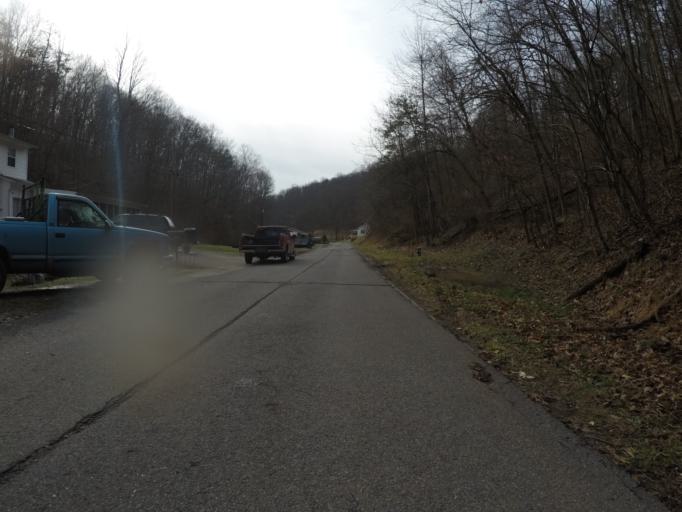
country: US
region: West Virginia
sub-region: Wayne County
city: Lavalette
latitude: 38.3341
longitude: -82.3772
